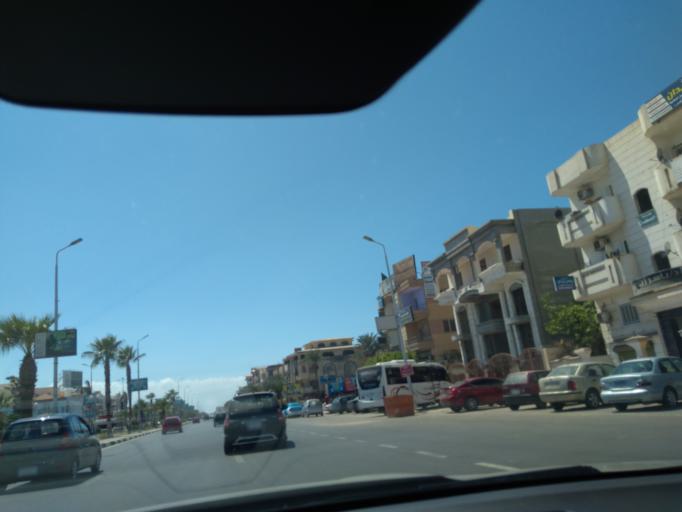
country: EG
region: Dumyat
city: Faraskur
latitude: 31.4420
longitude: 31.6845
